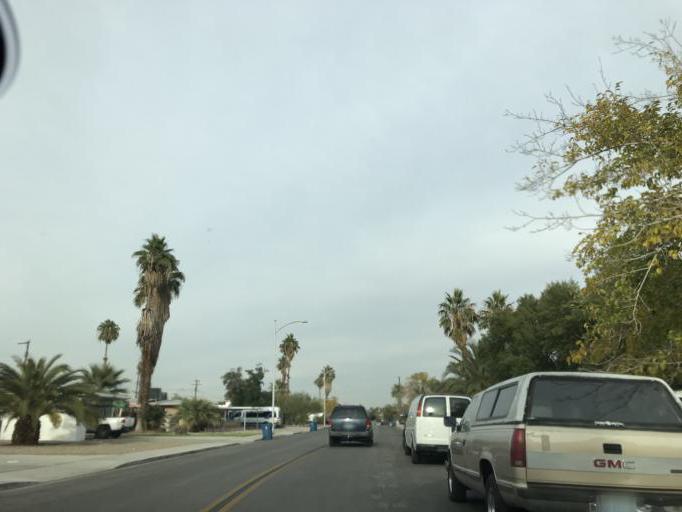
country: US
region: Nevada
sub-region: Clark County
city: Las Vegas
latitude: 36.1443
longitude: -115.1527
